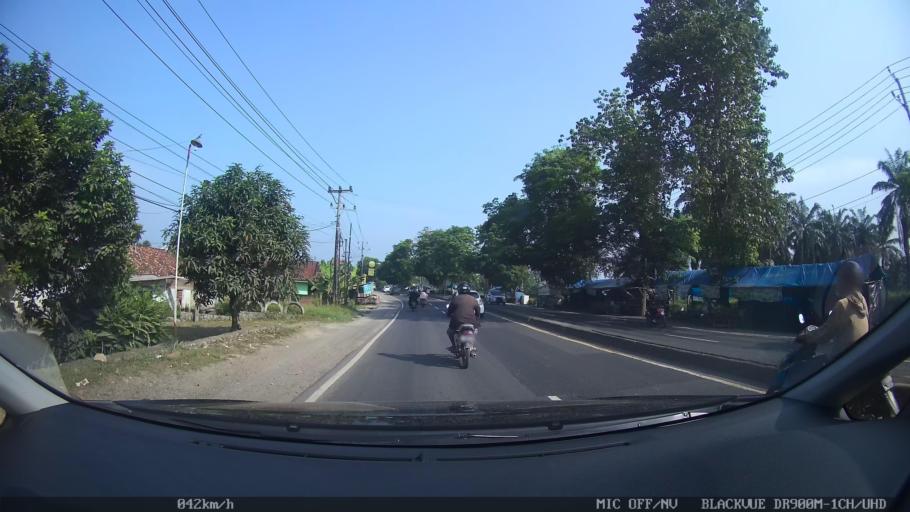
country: ID
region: Lampung
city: Natar
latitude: -5.3289
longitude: 105.2065
